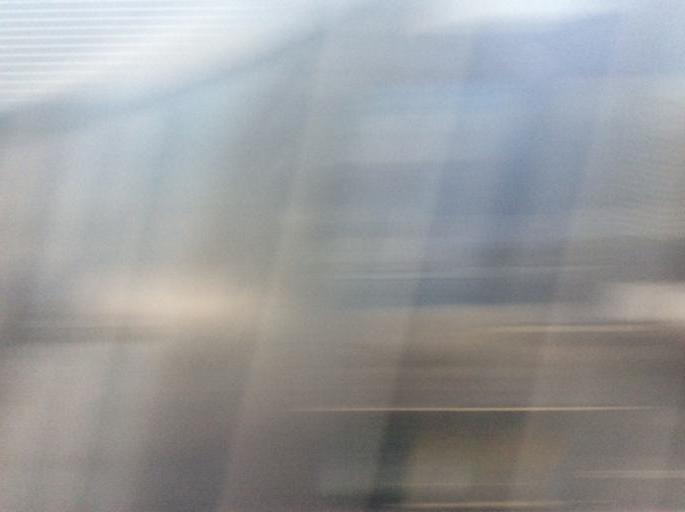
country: TW
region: Taiwan
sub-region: Tainan
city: Tainan
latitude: 22.9248
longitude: 120.2862
